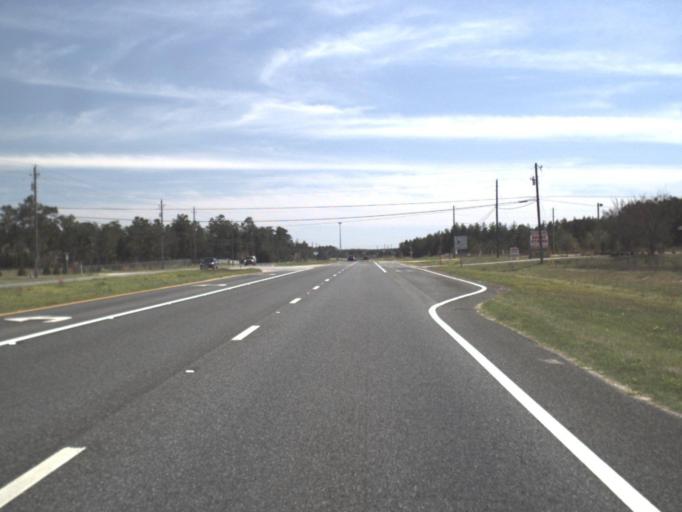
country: US
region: Florida
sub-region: Bay County
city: Lynn Haven
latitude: 30.4047
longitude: -85.6900
